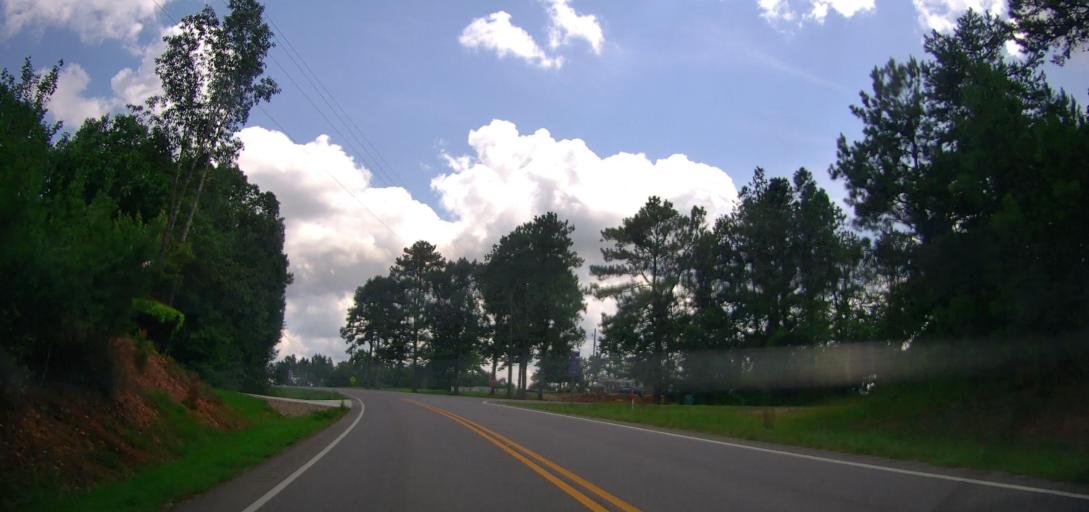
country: US
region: Alabama
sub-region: Cleburne County
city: Heflin
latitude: 33.6004
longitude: -85.4833
